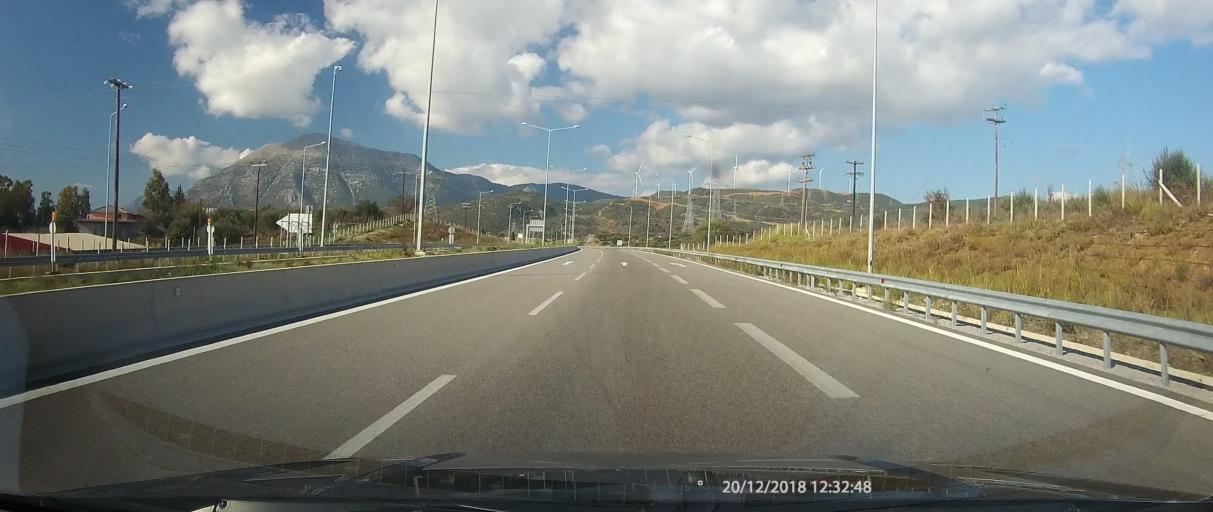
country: GR
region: West Greece
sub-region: Nomos Aitolias kai Akarnanias
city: Antirrio
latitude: 38.3438
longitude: 21.7579
